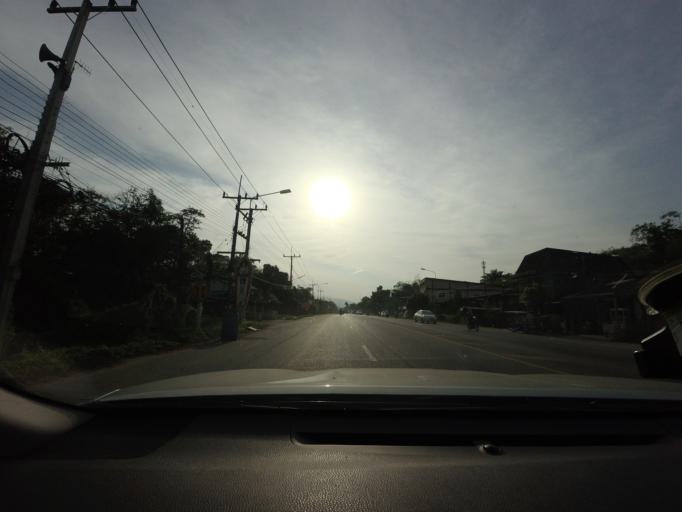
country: TH
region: Narathiwat
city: Ra-ngae
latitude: 6.2980
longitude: 101.7334
